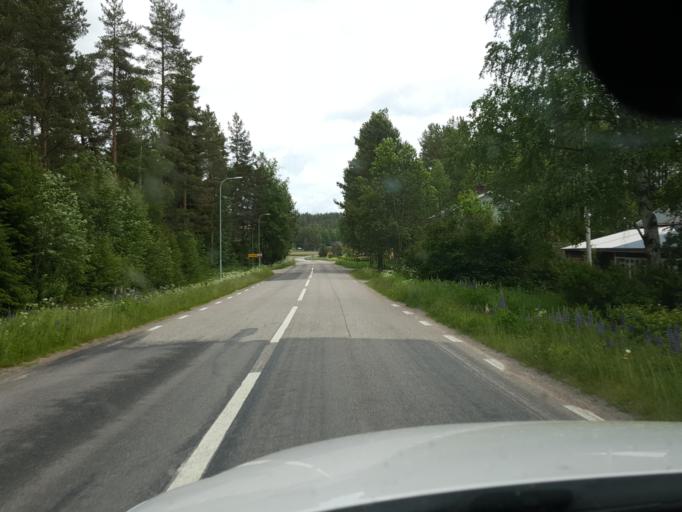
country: SE
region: Gaevleborg
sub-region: Ljusdals Kommun
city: Farila
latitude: 61.7941
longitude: 15.6472
